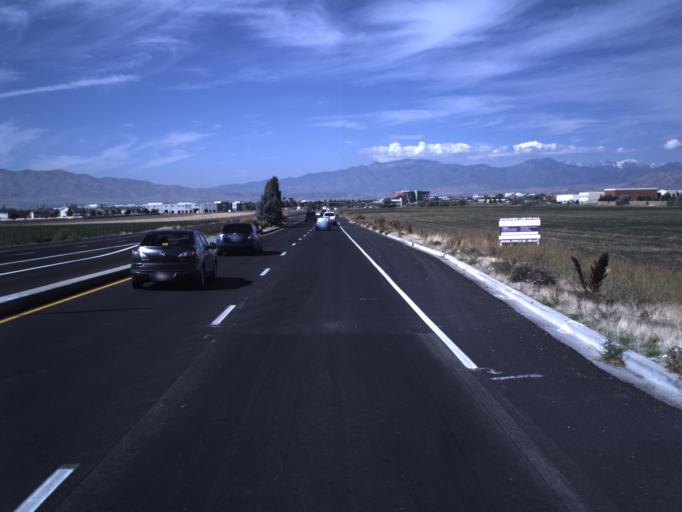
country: US
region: Utah
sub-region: Utah County
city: Pleasant Grove
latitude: 40.3509
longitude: -111.7441
